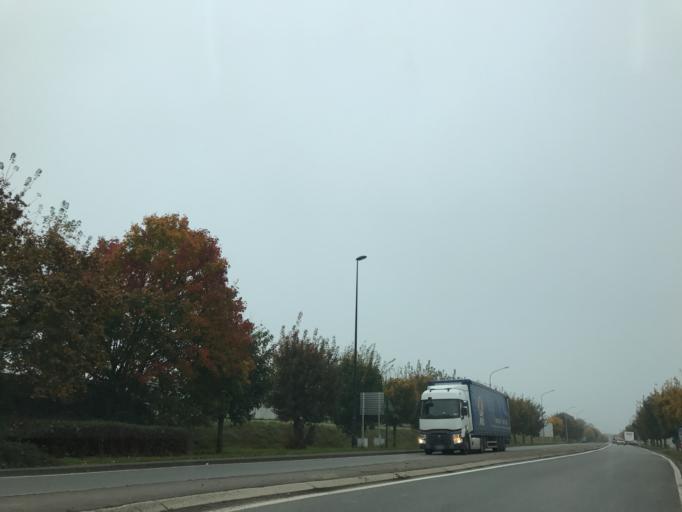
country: FR
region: Nord-Pas-de-Calais
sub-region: Departement du Pas-de-Calais
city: Bapaume
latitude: 50.1057
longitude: 2.8662
